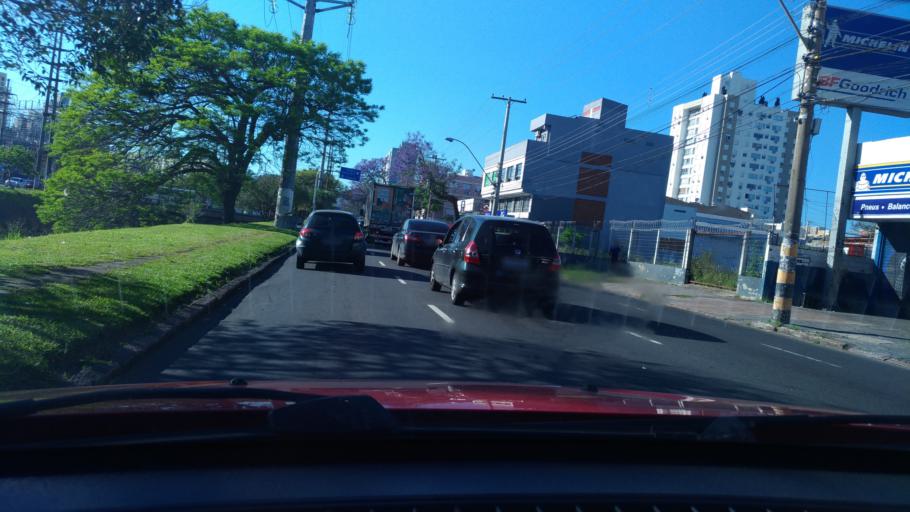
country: BR
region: Rio Grande do Sul
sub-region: Porto Alegre
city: Porto Alegre
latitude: -30.0456
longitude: -51.1987
